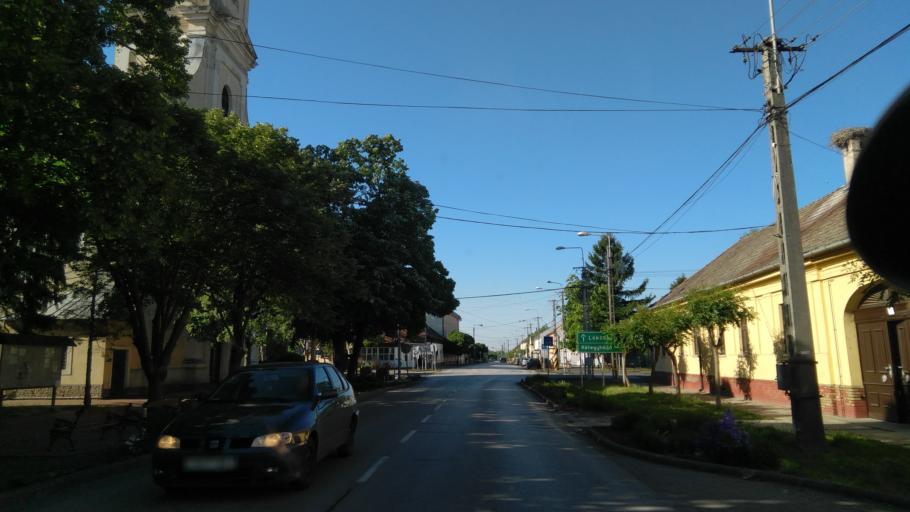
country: HU
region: Bekes
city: Elek
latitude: 46.5299
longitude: 21.2528
